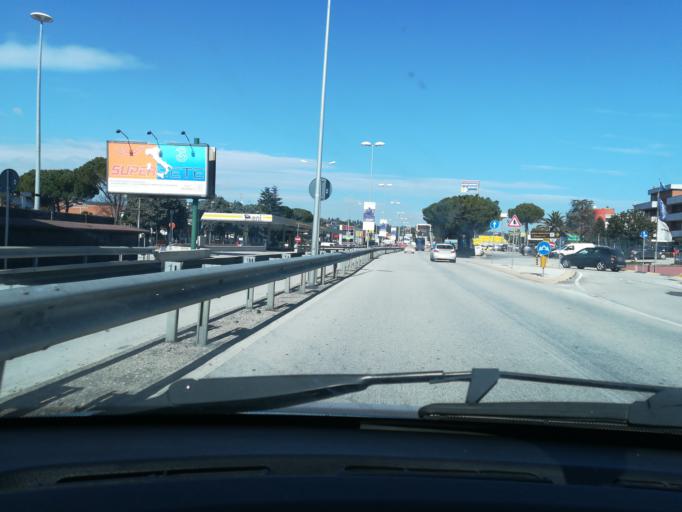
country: IT
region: The Marches
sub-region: Provincia di Macerata
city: Santa Maria Apparente
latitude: 43.2910
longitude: 13.7073
